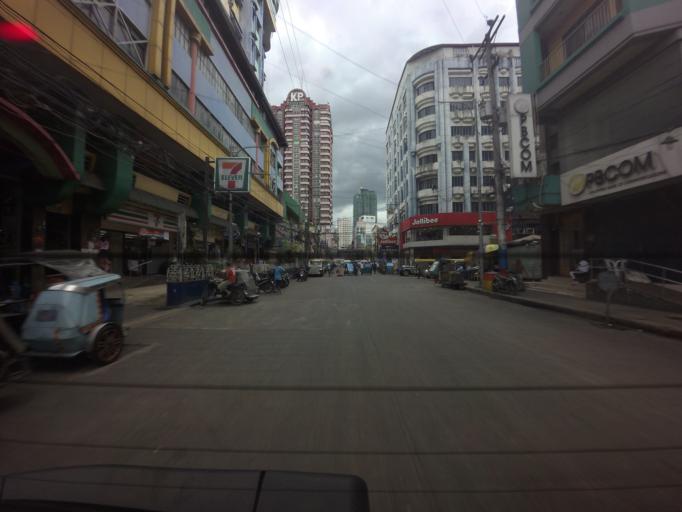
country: PH
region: Metro Manila
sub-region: City of Manila
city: Manila
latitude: 14.6067
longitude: 120.9698
